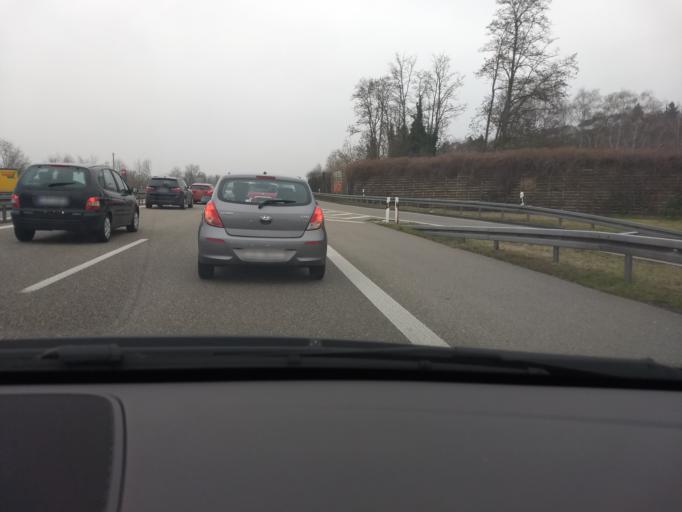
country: FR
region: Alsace
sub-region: Departement du Haut-Rhin
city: Kembs
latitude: 47.7072
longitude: 7.5256
